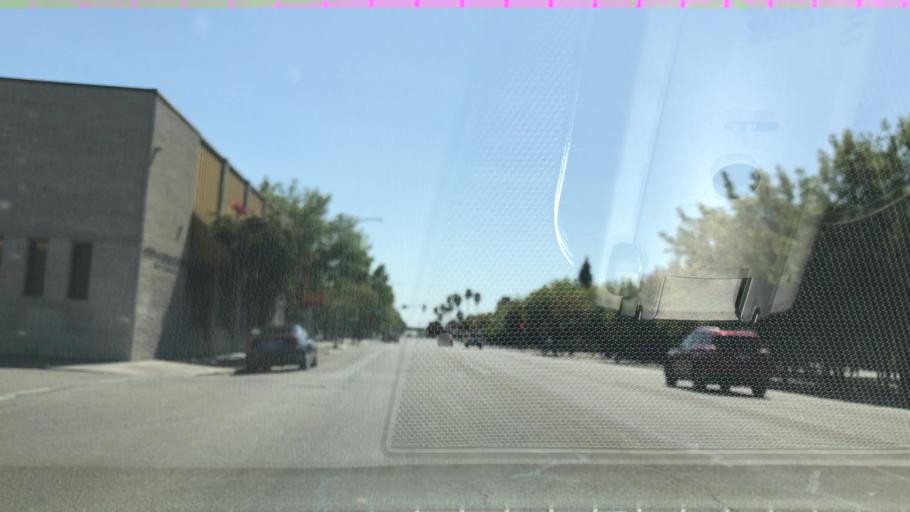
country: US
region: California
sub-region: San Joaquin County
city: Stockton
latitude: 37.9566
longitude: -121.2922
